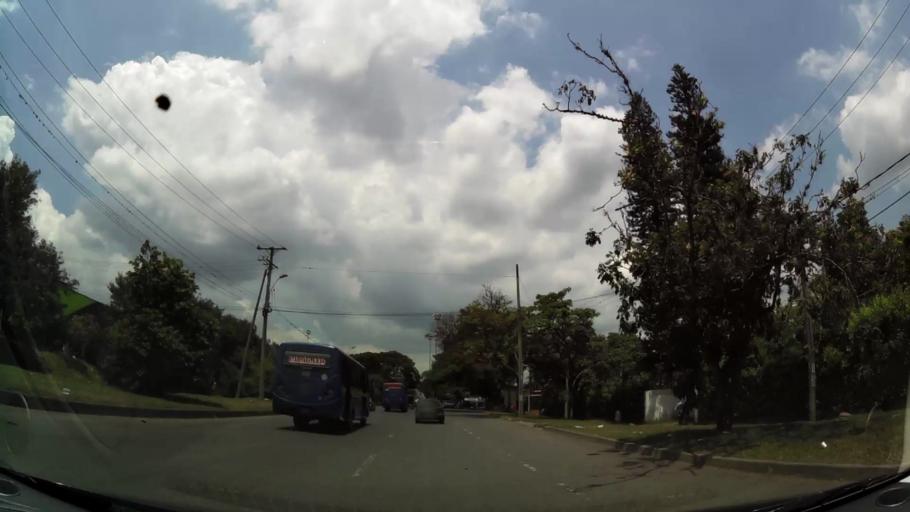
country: CO
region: Valle del Cauca
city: Cali
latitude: 3.4502
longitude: -76.4829
